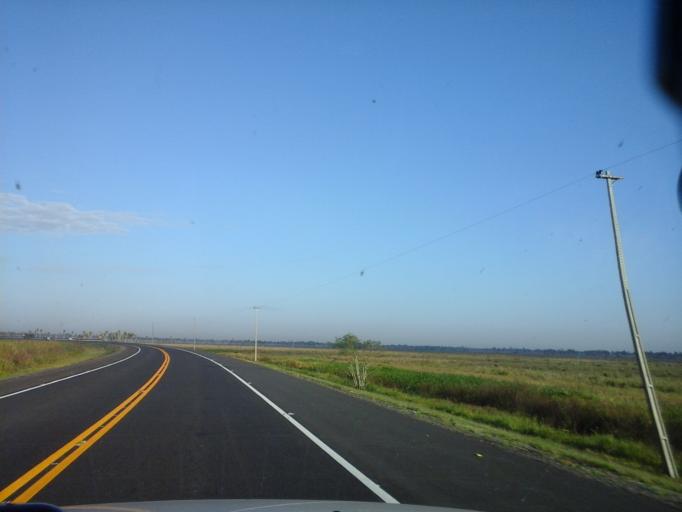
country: PY
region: Neembucu
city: Pilar
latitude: -26.8620
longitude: -57.8567
